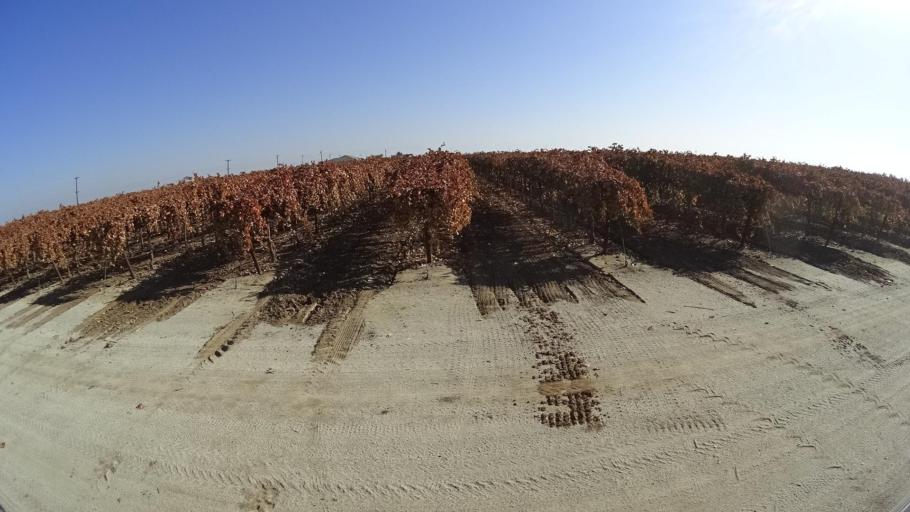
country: US
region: California
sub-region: Kern County
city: Delano
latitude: 35.7459
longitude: -119.2142
